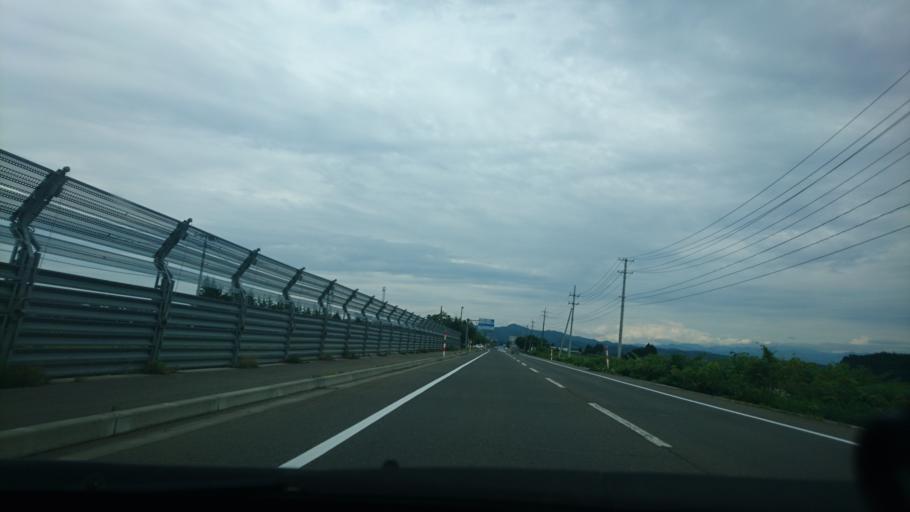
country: JP
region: Akita
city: Omagari
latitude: 39.5192
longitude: 140.3774
